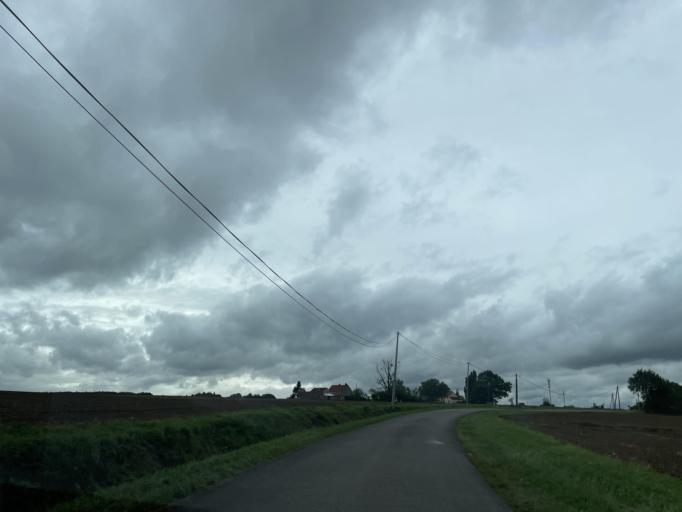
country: FR
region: Ile-de-France
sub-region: Departement de Seine-et-Marne
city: Chailly-en-Brie
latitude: 48.7818
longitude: 3.1615
